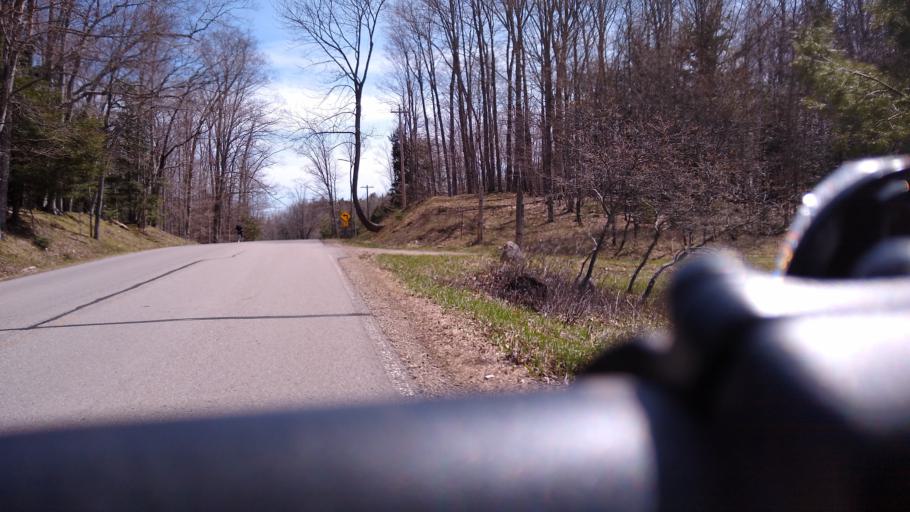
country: US
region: Michigan
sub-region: Delta County
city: Escanaba
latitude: 45.6973
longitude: -87.1629
